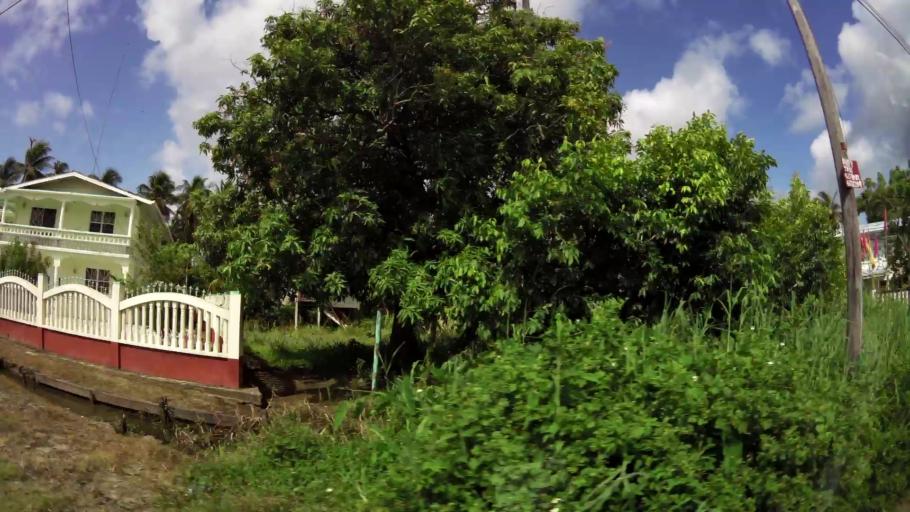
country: GY
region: Demerara-Mahaica
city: Mahaica Village
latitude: 6.7144
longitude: -57.9311
